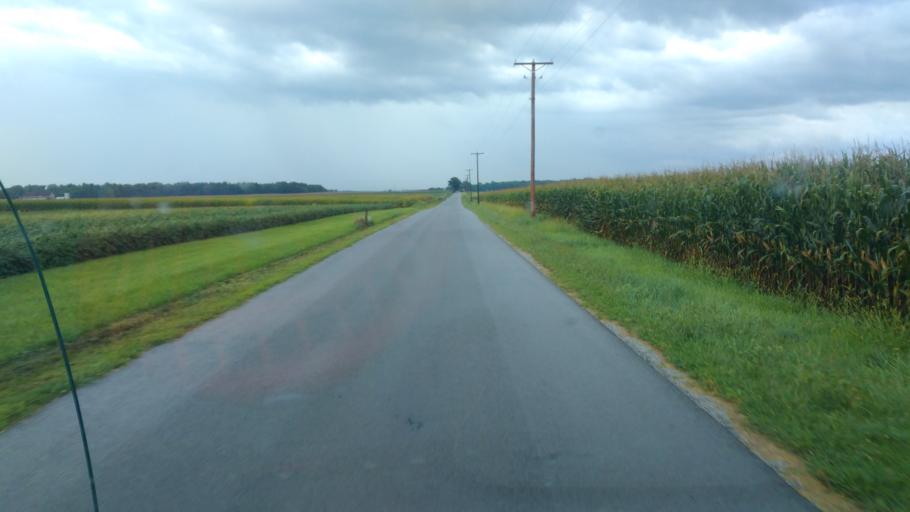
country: US
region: Ohio
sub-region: Hardin County
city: Kenton
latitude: 40.6893
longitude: -83.6257
